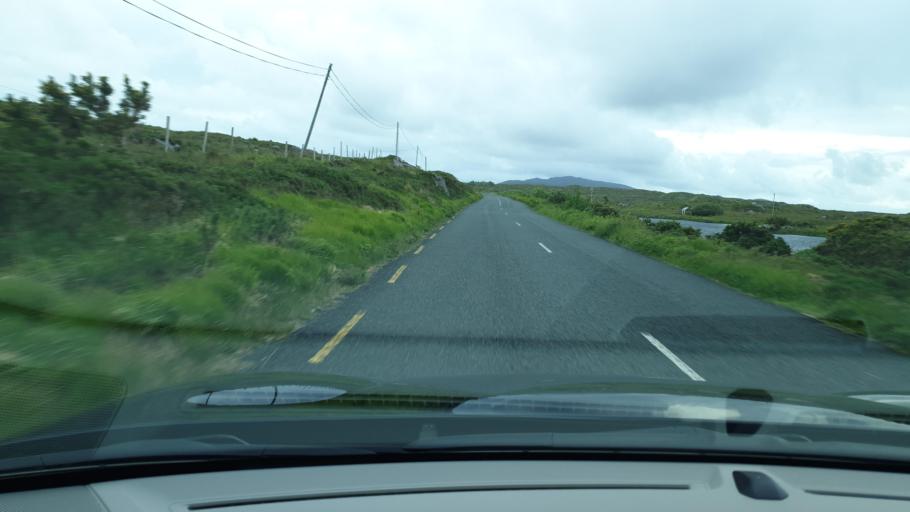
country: IE
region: Connaught
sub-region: County Galway
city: Clifden
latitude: 53.4469
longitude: -9.8762
